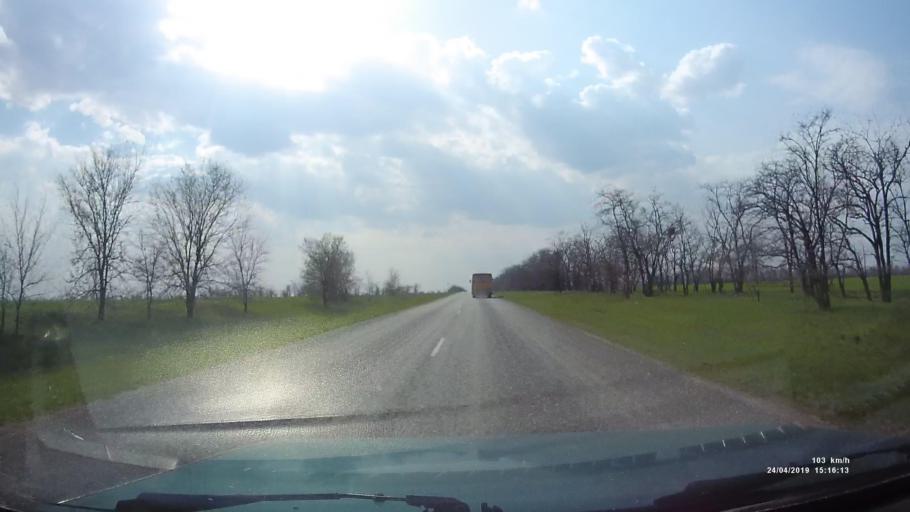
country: RU
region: Rostov
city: Remontnoye
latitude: 46.5449
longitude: 43.2192
